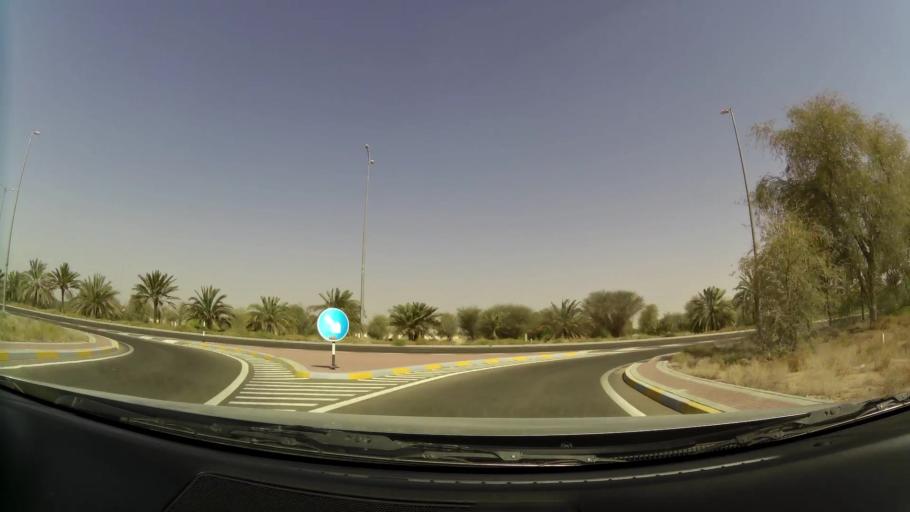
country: OM
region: Al Buraimi
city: Al Buraymi
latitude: 24.3066
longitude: 55.7941
